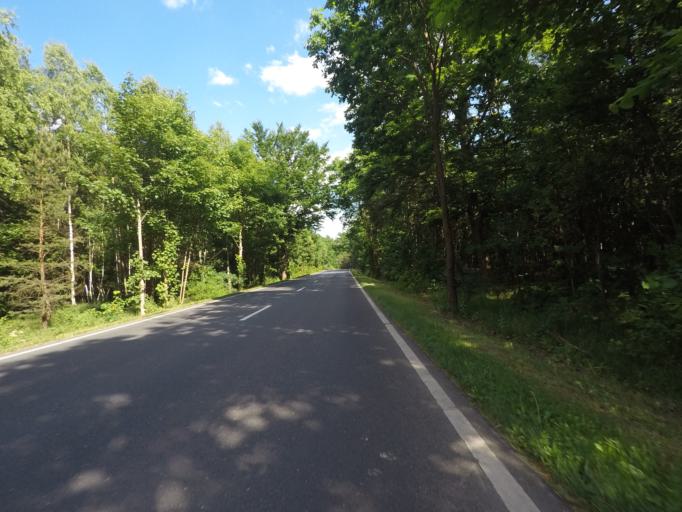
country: DE
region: Brandenburg
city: Britz
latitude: 52.8585
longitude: 13.7939
